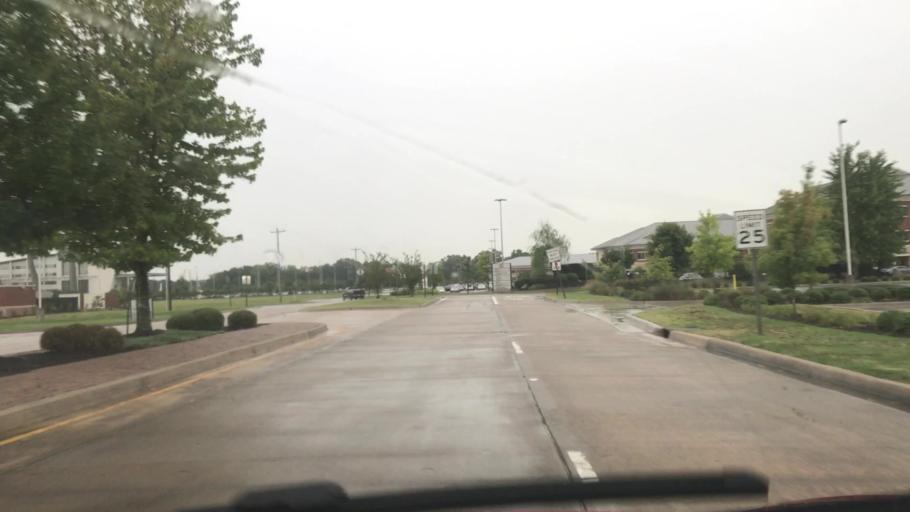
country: US
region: Louisiana
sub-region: Bossier Parish
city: Red Chute
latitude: 32.5413
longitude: -93.6461
